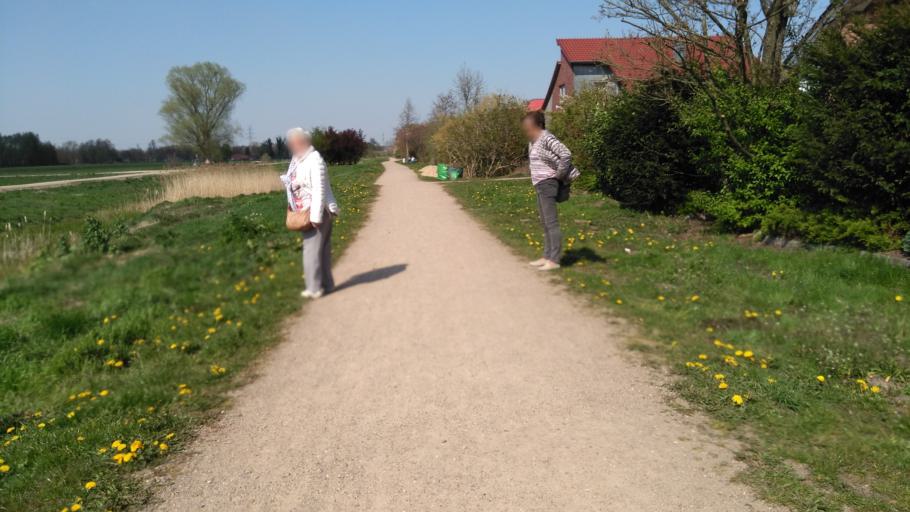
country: DE
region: Lower Saxony
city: Buxtehude
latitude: 53.4780
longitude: 9.6820
